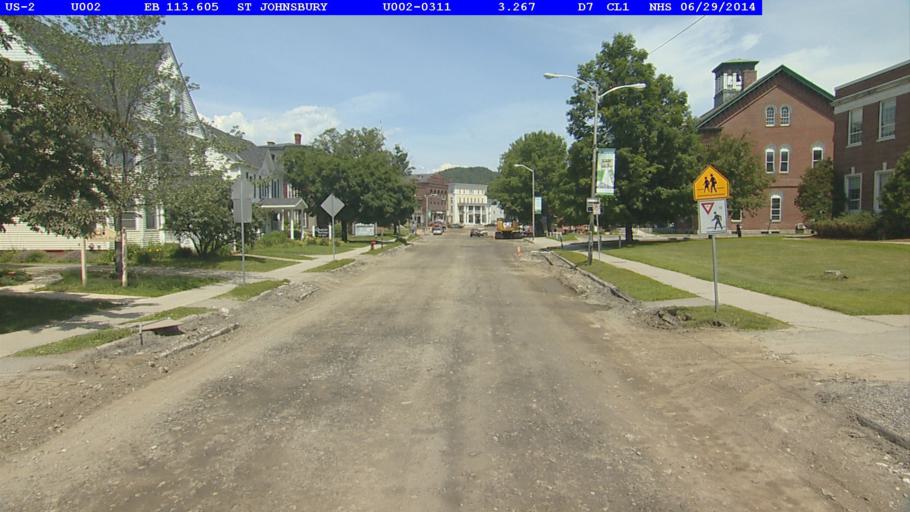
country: US
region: Vermont
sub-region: Caledonia County
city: Saint Johnsbury
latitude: 44.4173
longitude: -72.0203
